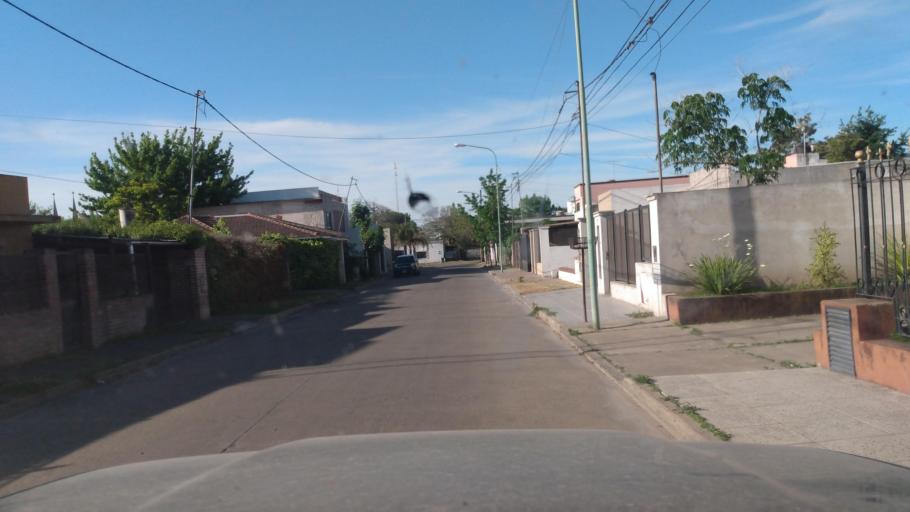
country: AR
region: Buenos Aires
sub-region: Partido de Lujan
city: Lujan
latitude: -34.5730
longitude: -59.1200
